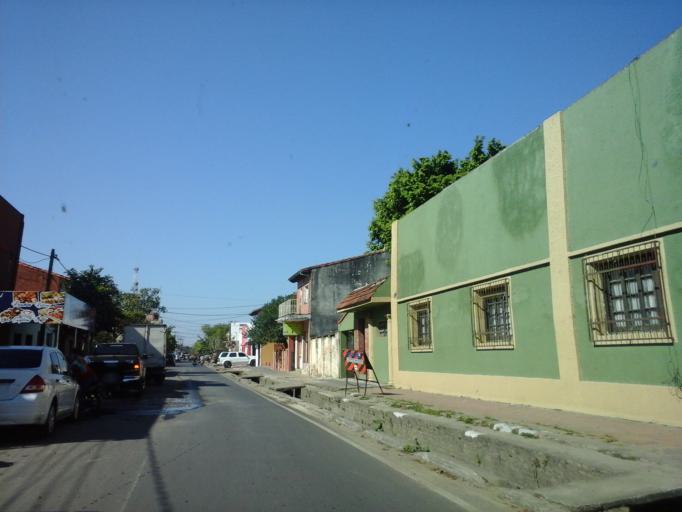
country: PY
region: Neembucu
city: Pilar
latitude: -26.8601
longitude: -58.3020
